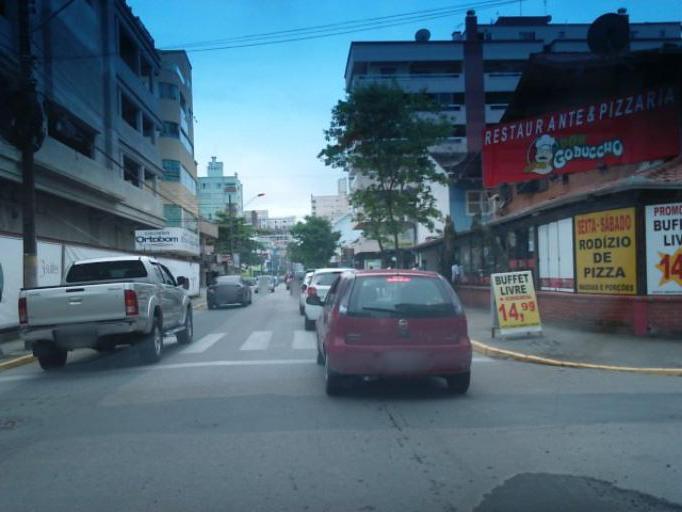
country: BR
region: Santa Catarina
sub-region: Itapema
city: Itapema
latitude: -27.1328
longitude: -48.6016
